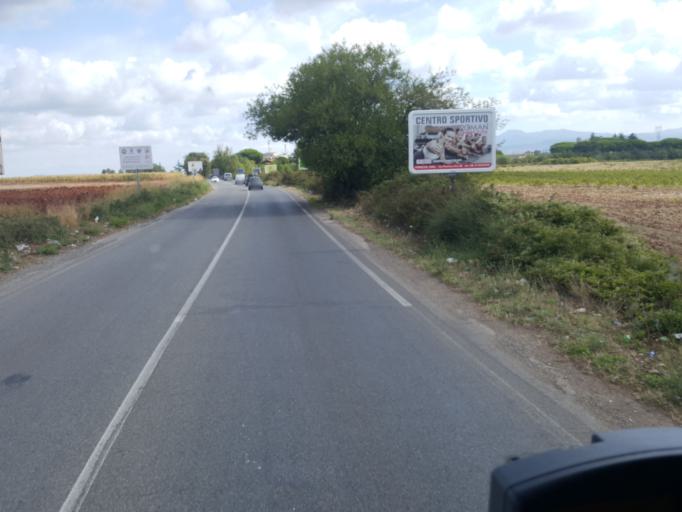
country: IT
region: Latium
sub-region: Citta metropolitana di Roma Capitale
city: Area Produttiva
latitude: 41.6919
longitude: 12.5194
